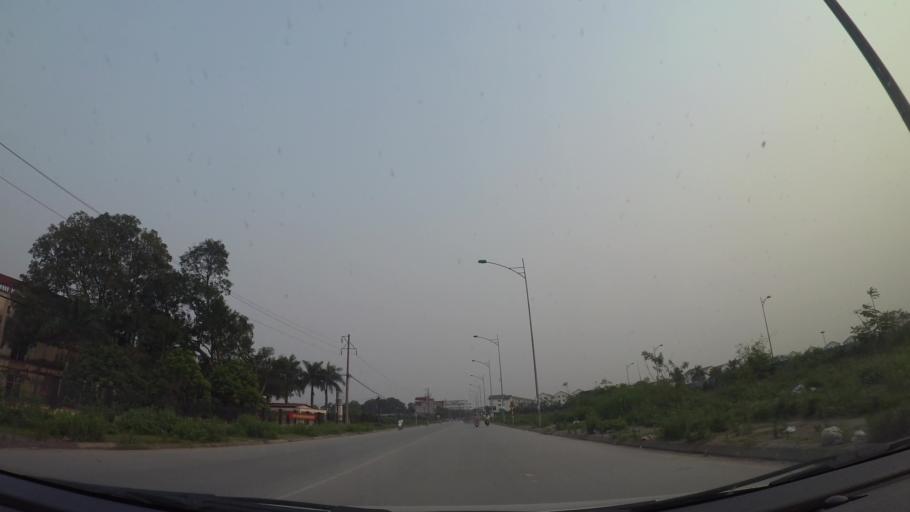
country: VN
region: Ha Noi
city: Cau Dien
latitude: 21.0014
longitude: 105.7240
